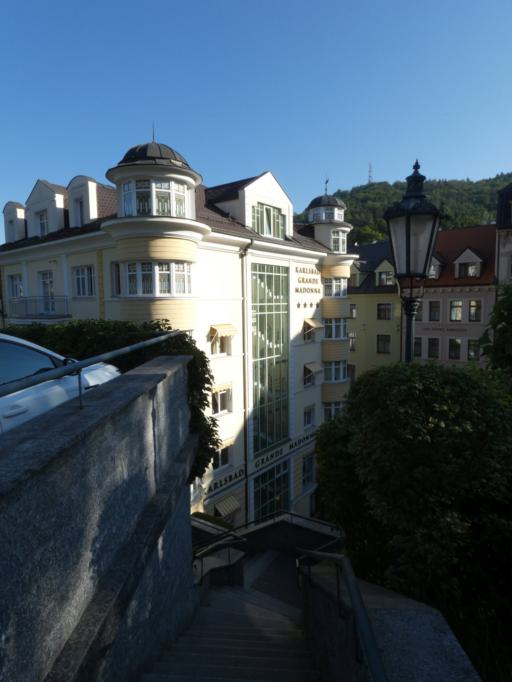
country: CZ
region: Karlovarsky
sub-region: Okres Karlovy Vary
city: Karlovy Vary
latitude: 50.2220
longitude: 12.8849
